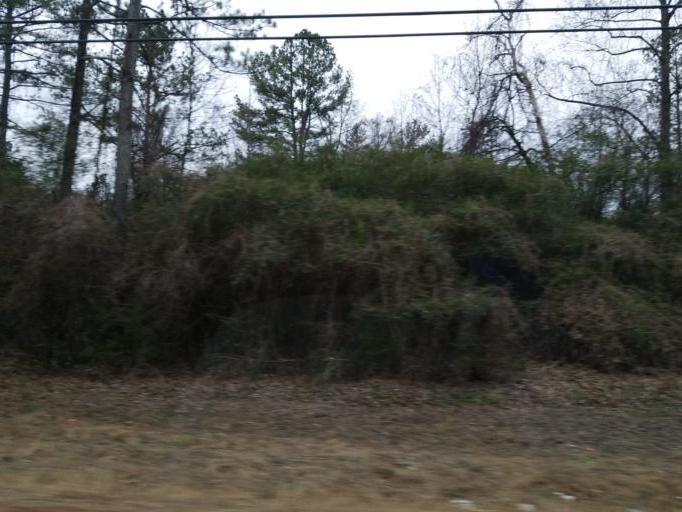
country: US
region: Georgia
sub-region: Dawson County
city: Dawsonville
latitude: 34.4970
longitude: -84.2006
